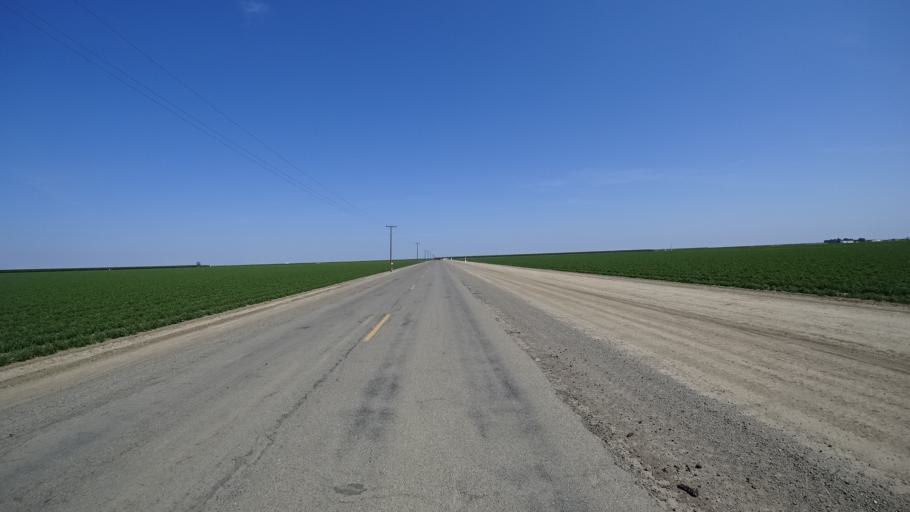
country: US
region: California
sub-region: Fresno County
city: Huron
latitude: 36.1269
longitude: -120.0037
